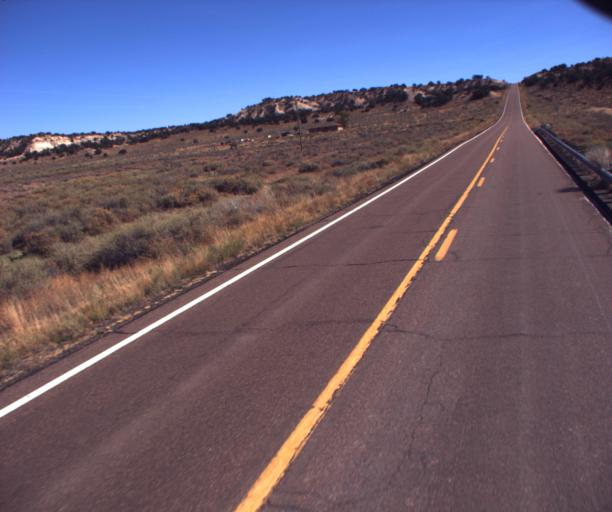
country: US
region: Arizona
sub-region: Navajo County
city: First Mesa
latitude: 35.7621
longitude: -109.9728
